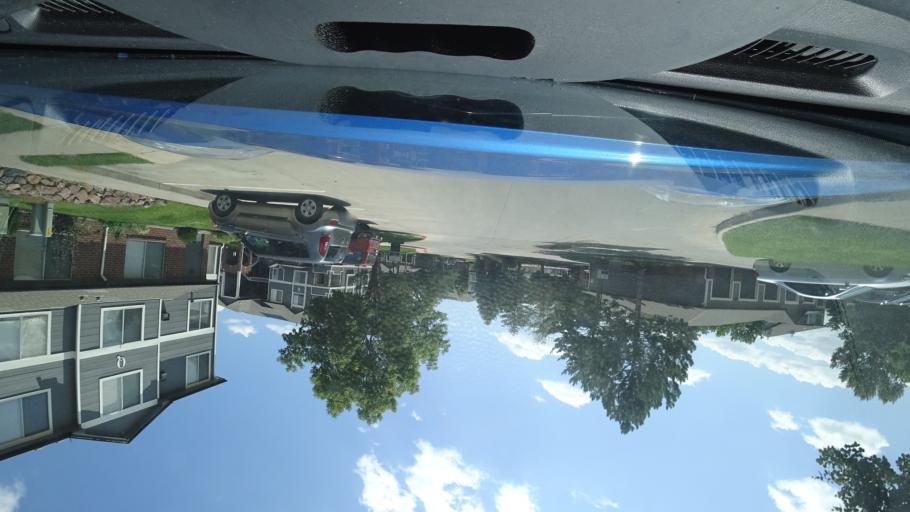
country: US
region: Colorado
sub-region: Arapahoe County
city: Glendale
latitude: 39.7003
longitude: -104.8908
